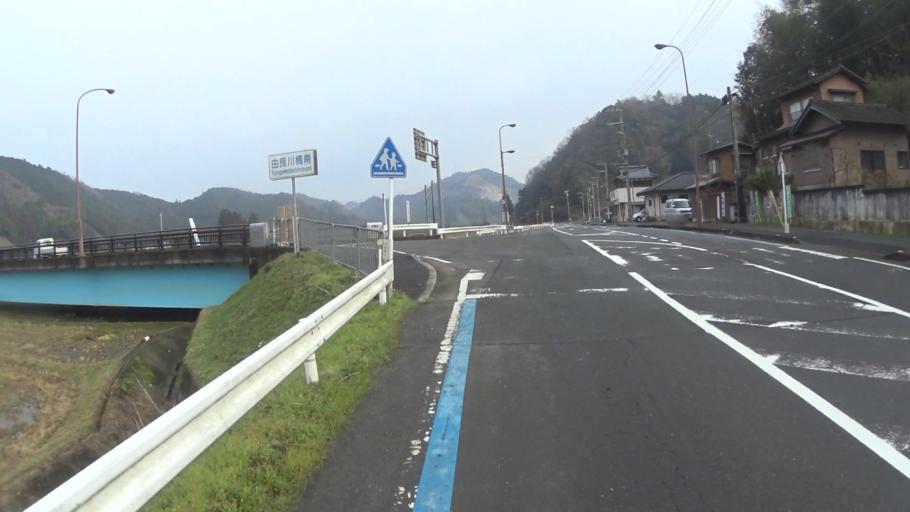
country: JP
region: Kyoto
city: Miyazu
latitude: 35.4233
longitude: 135.2196
